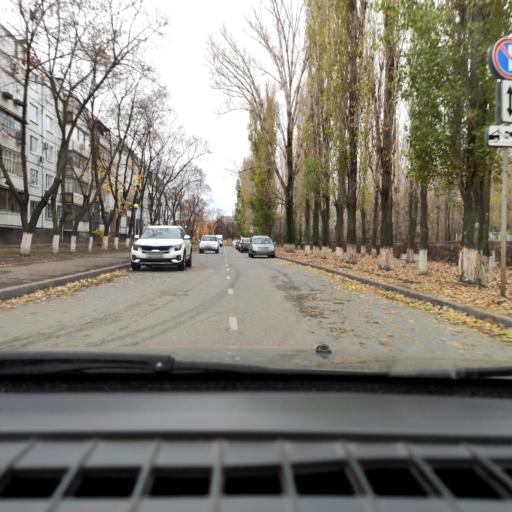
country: RU
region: Samara
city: Tol'yatti
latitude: 53.5214
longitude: 49.2853
